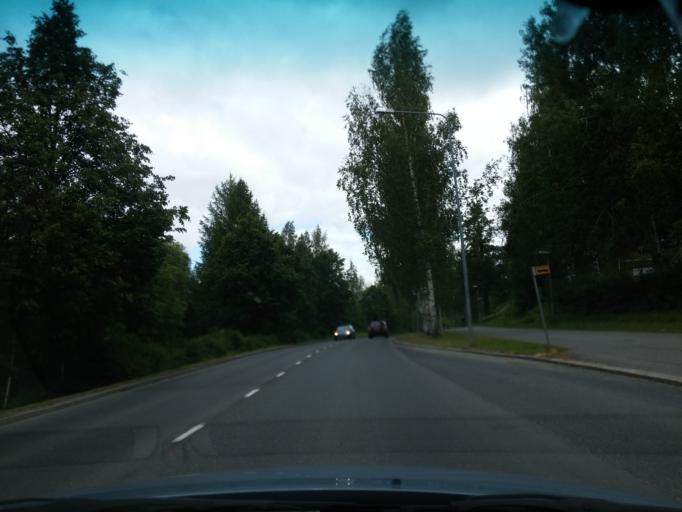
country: FI
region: Northern Savo
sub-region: Kuopio
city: Kuopio
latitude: 62.8357
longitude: 27.6115
